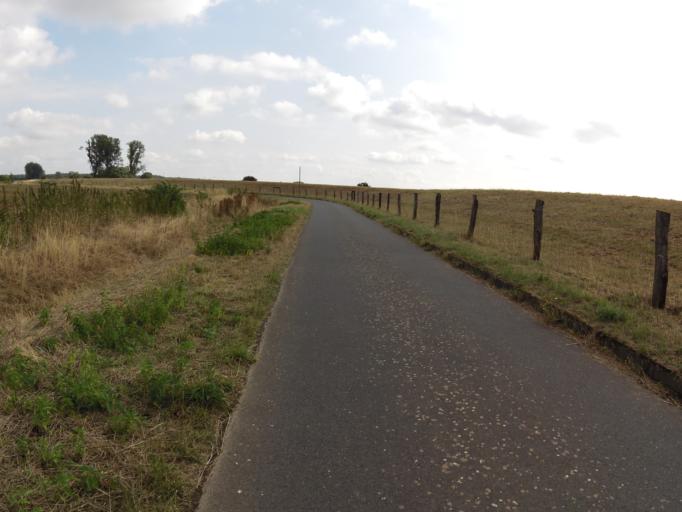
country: DE
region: Lower Saxony
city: Hoya
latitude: 52.8140
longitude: 9.1666
